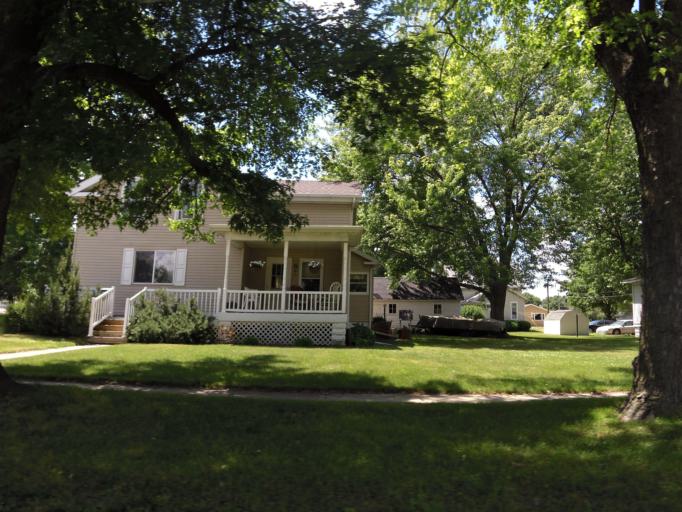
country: US
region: Iowa
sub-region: Buchanan County
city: Independence
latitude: 42.4728
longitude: -91.8894
